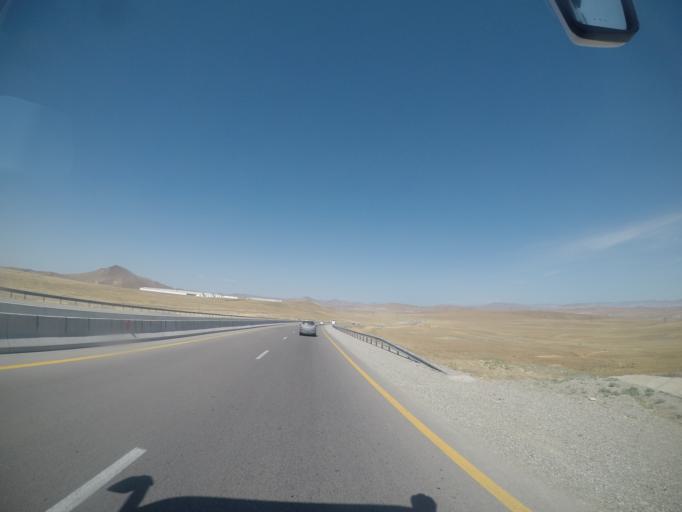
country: AZ
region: Sumqayit
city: Haci Zeynalabdin
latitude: 40.4849
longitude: 49.4112
